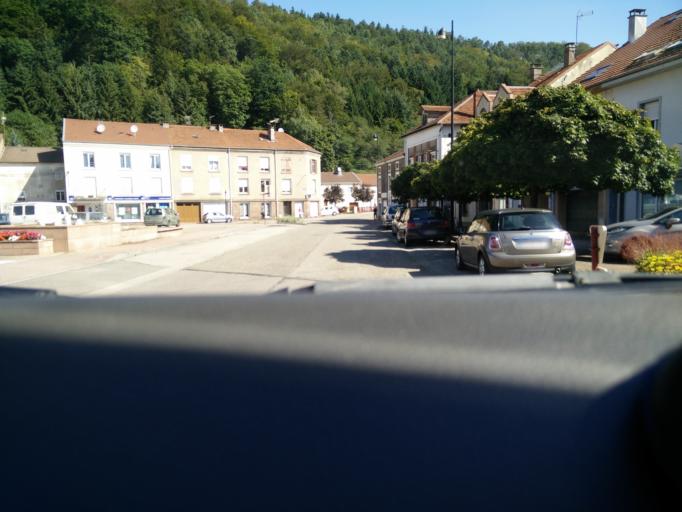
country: FR
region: Lorraine
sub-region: Departement des Vosges
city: Etival-Clairefontaine
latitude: 48.4081
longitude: 6.8447
